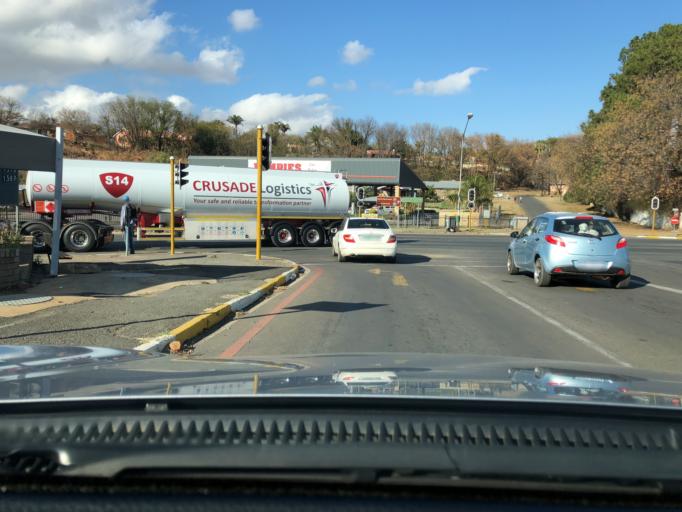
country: ZA
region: KwaZulu-Natal
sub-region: uThukela District Municipality
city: Ladysmith
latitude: -28.5569
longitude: 29.7726
